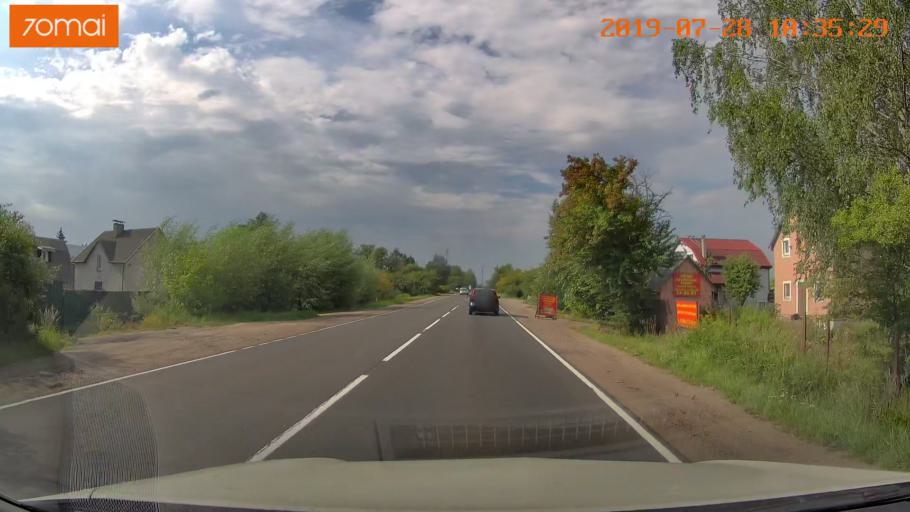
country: RU
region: Kaliningrad
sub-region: Gorod Kaliningrad
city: Kaliningrad
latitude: 54.7463
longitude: 20.4311
